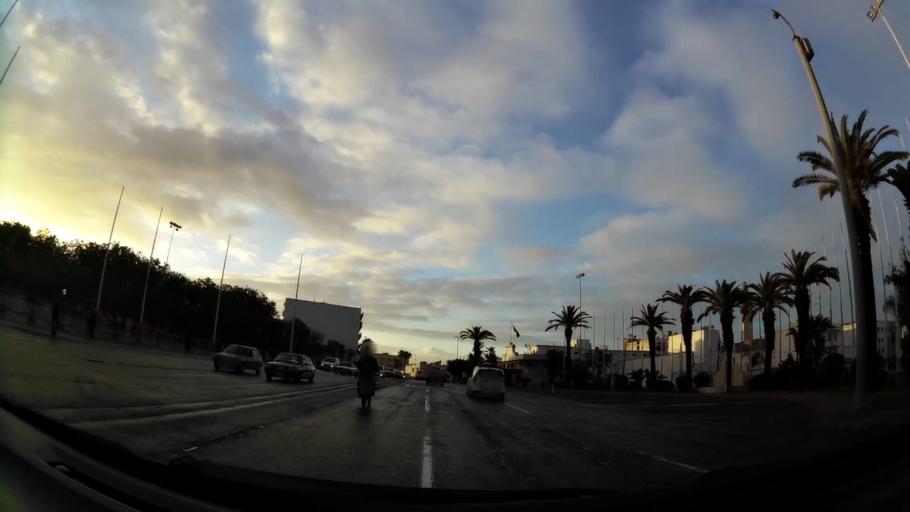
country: MA
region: Grand Casablanca
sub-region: Casablanca
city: Casablanca
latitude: 33.5809
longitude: -7.6018
